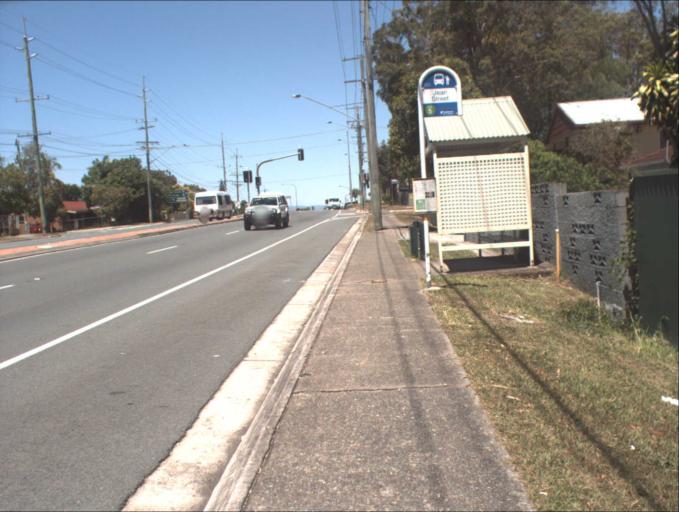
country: AU
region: Queensland
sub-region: Logan
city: Logan City
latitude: -27.6365
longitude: 153.1187
